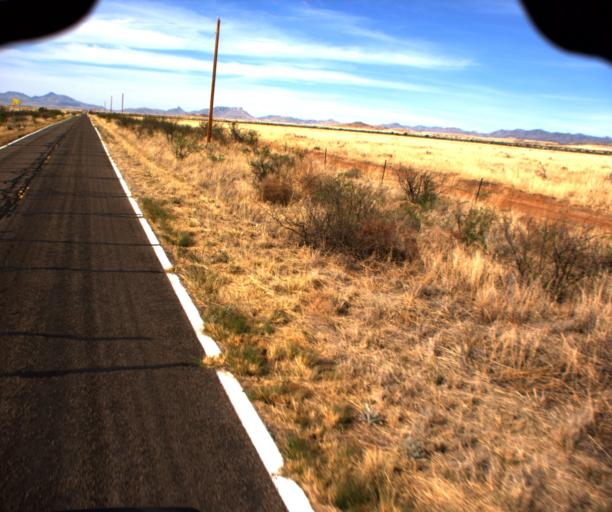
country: US
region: Arizona
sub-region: Cochise County
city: Willcox
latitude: 31.9013
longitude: -109.4914
